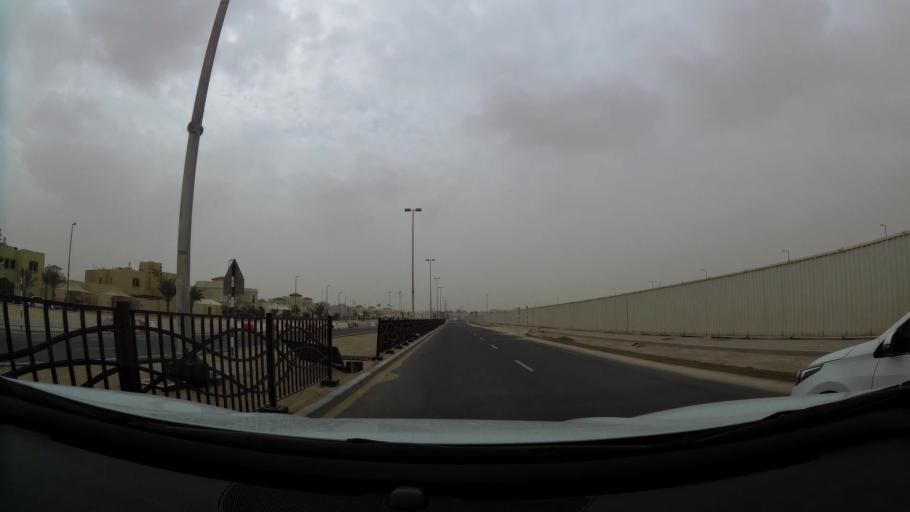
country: AE
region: Abu Dhabi
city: Abu Dhabi
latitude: 24.4342
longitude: 54.7267
